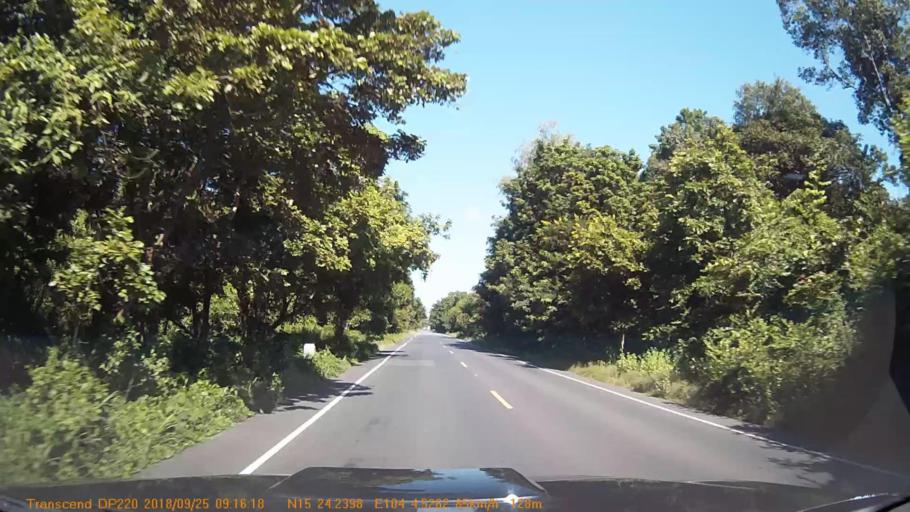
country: TH
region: Sisaket
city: Sila Lat
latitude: 15.4039
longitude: 104.0755
